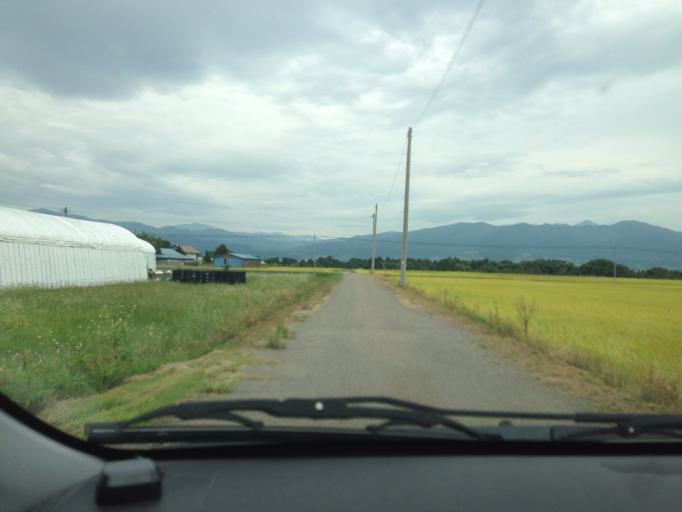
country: JP
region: Fukushima
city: Kitakata
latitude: 37.6324
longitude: 139.8453
